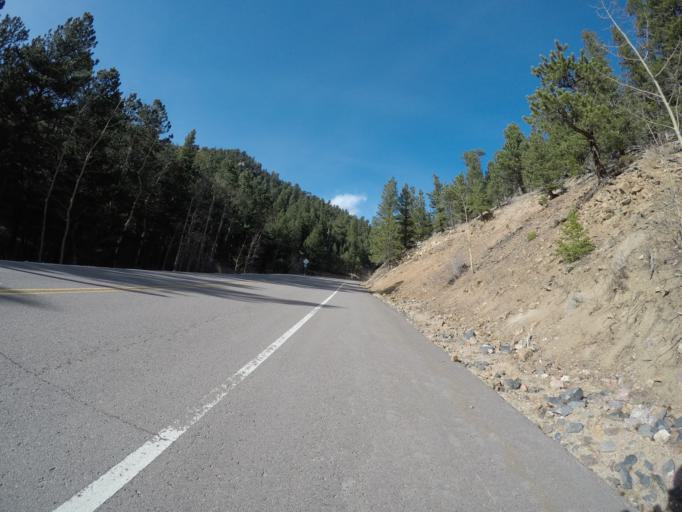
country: US
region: Colorado
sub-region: Boulder County
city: Nederland
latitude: 40.0566
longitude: -105.5013
